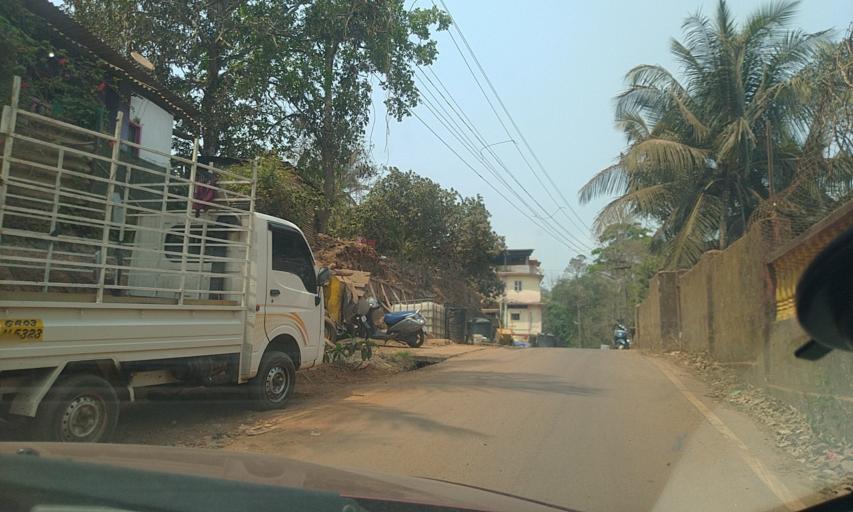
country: IN
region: Goa
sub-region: North Goa
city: Serula
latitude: 15.5215
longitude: 73.8399
